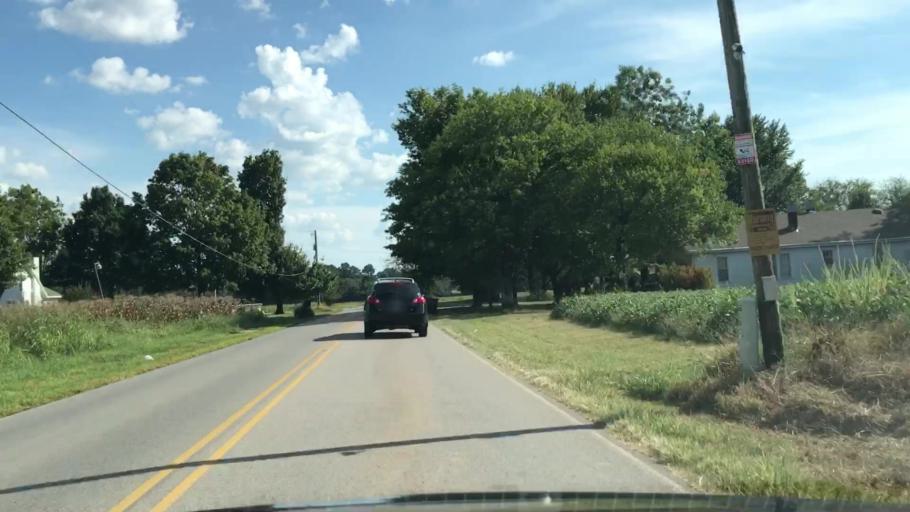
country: US
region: Alabama
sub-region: Madison County
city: Harvest
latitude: 34.8683
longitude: -86.7490
